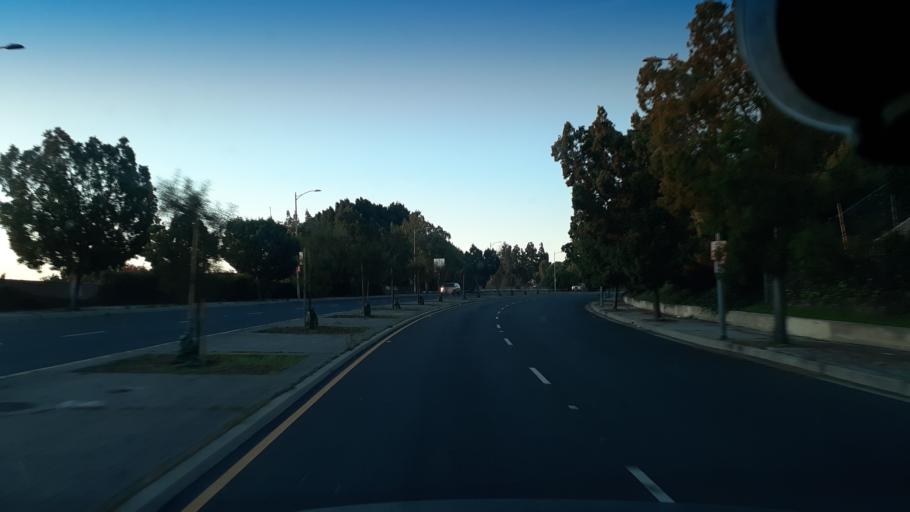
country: US
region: California
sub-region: Los Angeles County
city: San Pedro
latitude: 33.7409
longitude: -118.3107
